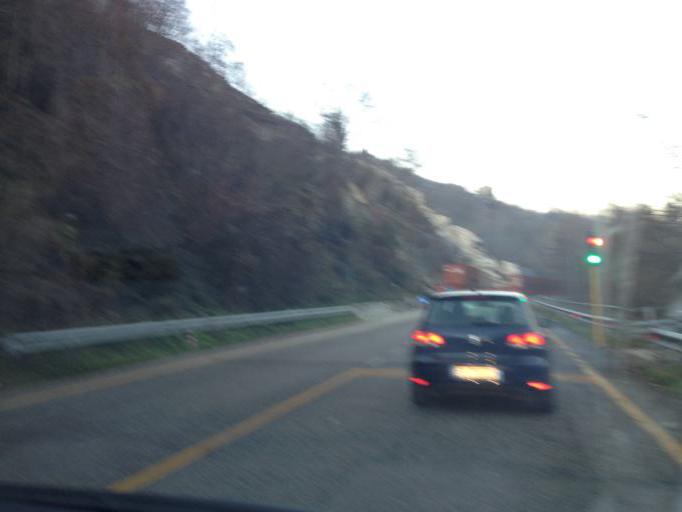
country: IT
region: The Marches
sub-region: Provincia di Ascoli Piceno
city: Arquata del Tronto
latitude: 42.7493
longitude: 13.2715
